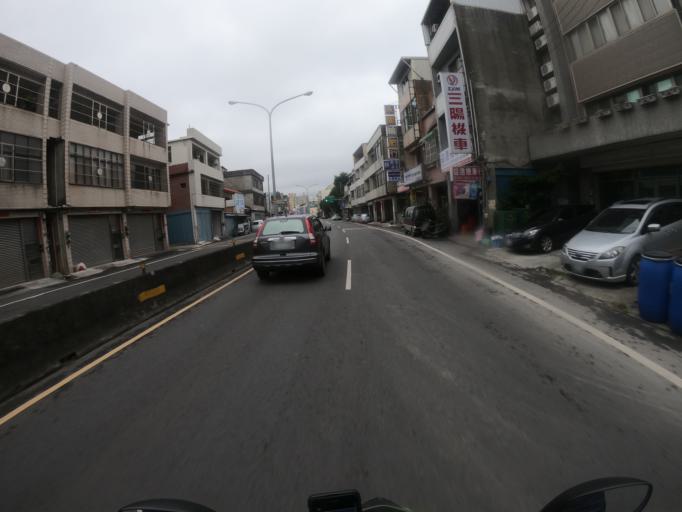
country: TW
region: Taiwan
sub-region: Hsinchu
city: Zhubei
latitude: 24.8234
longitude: 121.0093
